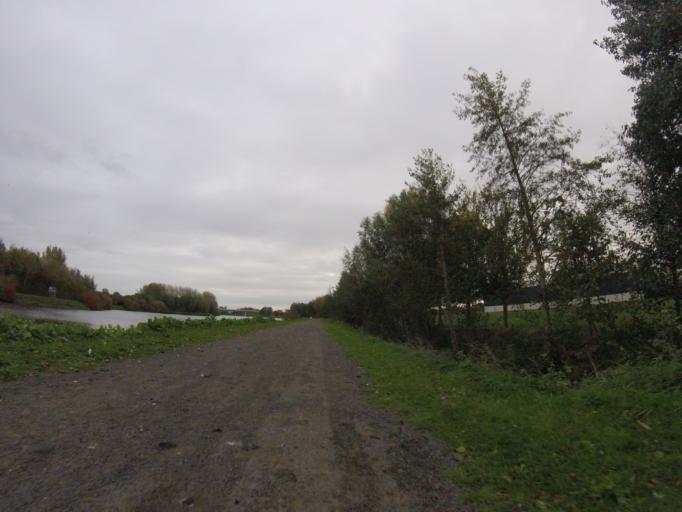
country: FR
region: Nord-Pas-de-Calais
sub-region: Departement du Nord
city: Quesnoy-sur-Deule
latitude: 50.6997
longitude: 3.0182
